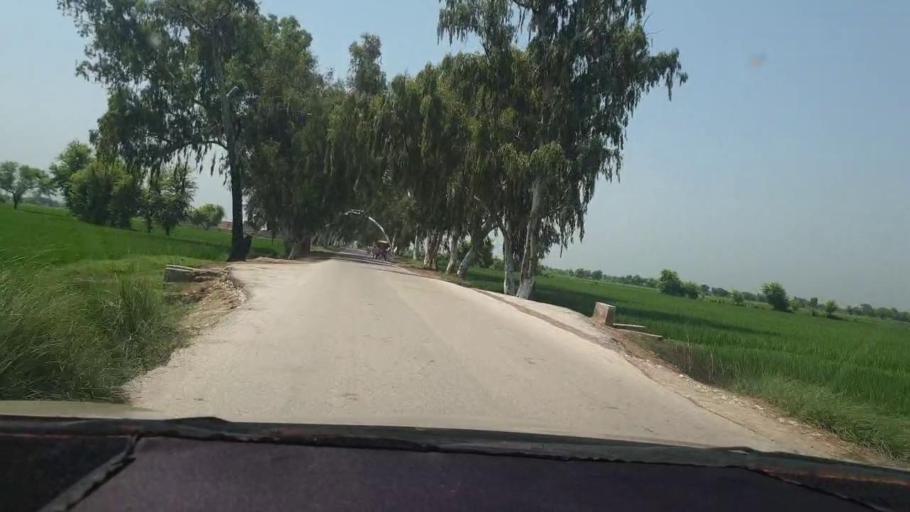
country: PK
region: Sindh
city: Kambar
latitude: 27.6053
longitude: 68.0371
